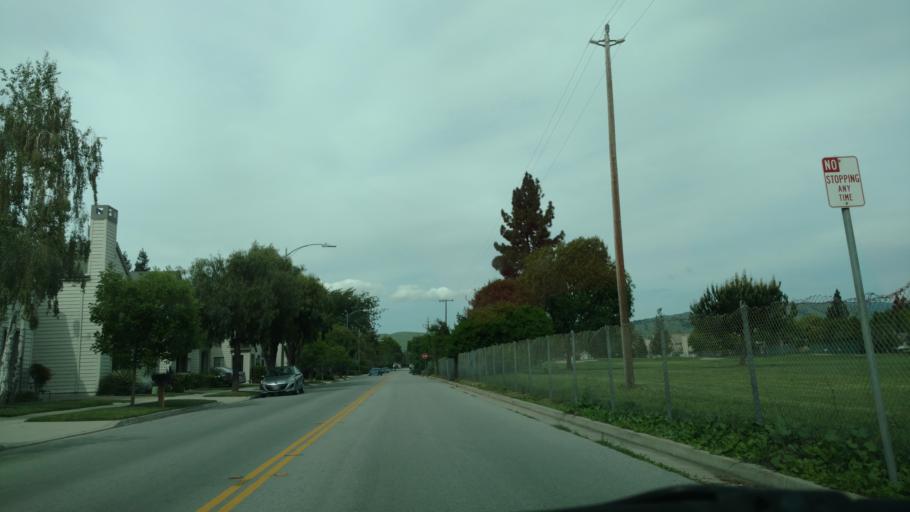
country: US
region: California
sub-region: Santa Clara County
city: San Jose
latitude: 37.3811
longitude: -121.8888
